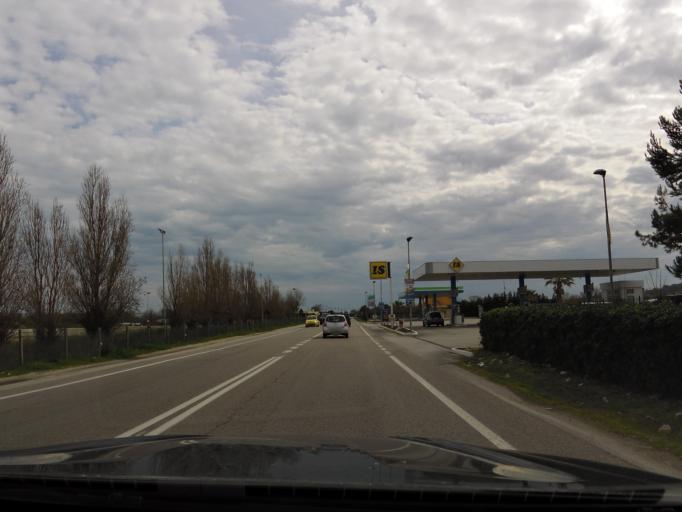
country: IT
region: The Marches
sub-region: Provincia di Macerata
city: Porto Potenza Picena
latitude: 43.3905
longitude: 13.6829
